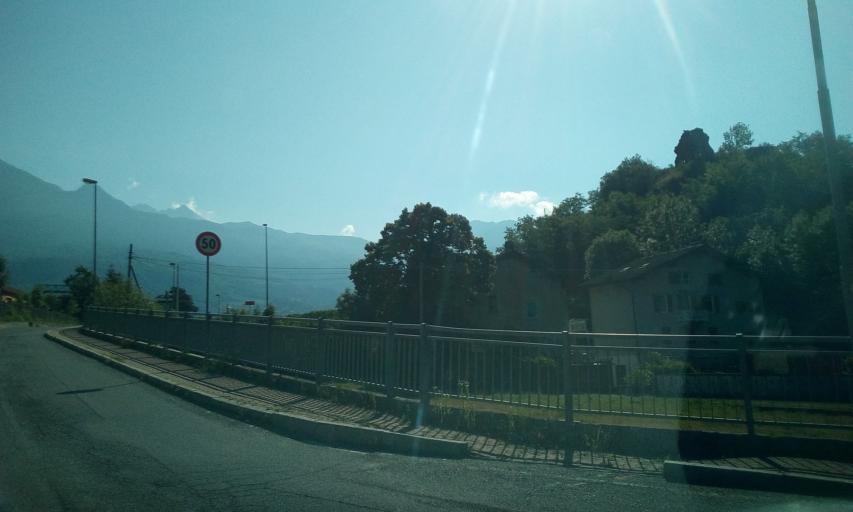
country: IT
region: Aosta Valley
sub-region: Valle d'Aosta
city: Chatillon
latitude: 45.7428
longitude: 7.6179
